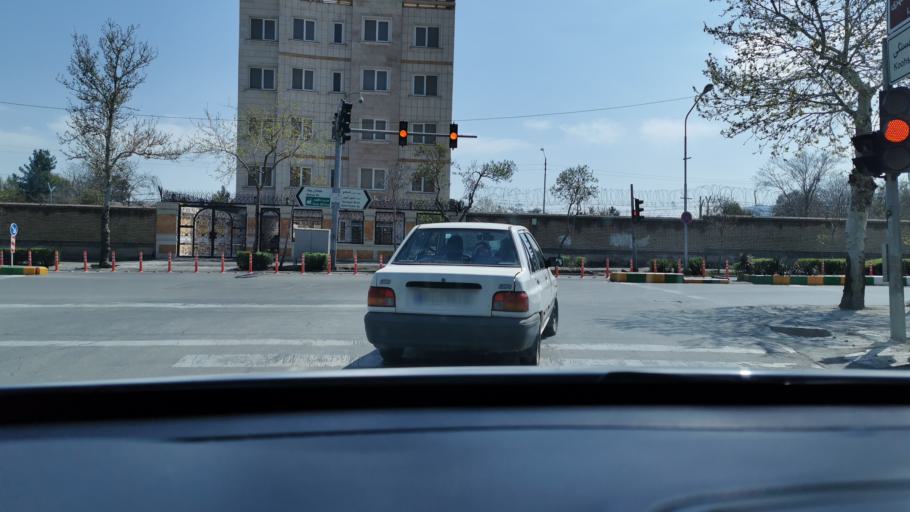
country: IR
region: Razavi Khorasan
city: Mashhad
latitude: 36.2853
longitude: 59.5793
